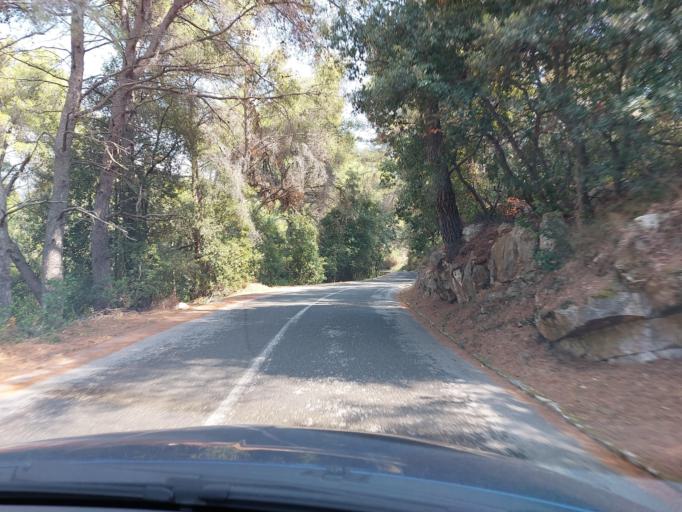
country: HR
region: Dubrovacko-Neretvanska
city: Smokvica
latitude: 42.7668
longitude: 16.8860
